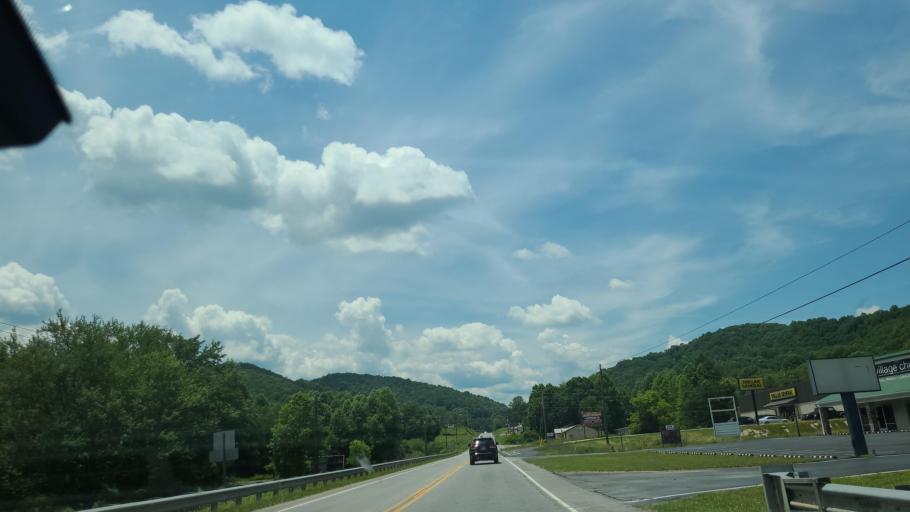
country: US
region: North Carolina
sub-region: Clay County
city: Hayesville
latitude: 35.0336
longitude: -83.8484
